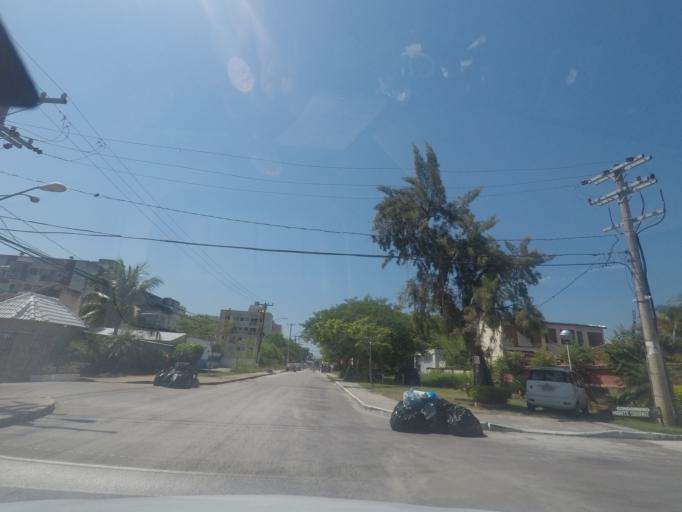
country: BR
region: Rio de Janeiro
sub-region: Nilopolis
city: Nilopolis
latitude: -22.9890
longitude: -43.4763
